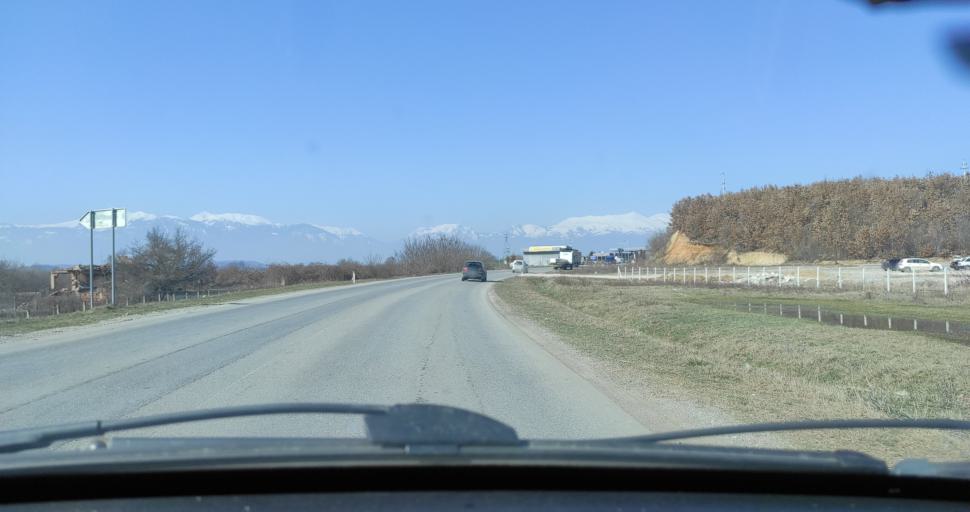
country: XK
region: Pec
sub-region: Komuna e Pejes
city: Kosuriq
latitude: 42.6072
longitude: 20.5095
